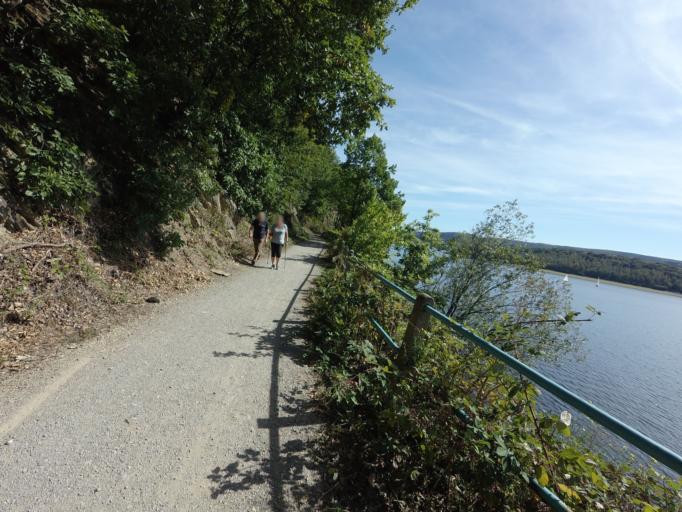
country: DE
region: North Rhine-Westphalia
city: Heimbach
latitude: 50.6510
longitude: 6.4237
